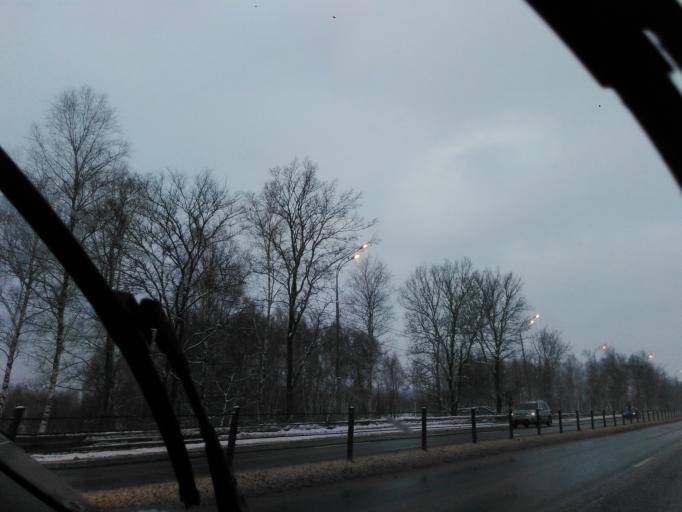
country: RU
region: Moskovskaya
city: Dedenevo
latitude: 56.2643
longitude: 37.5031
